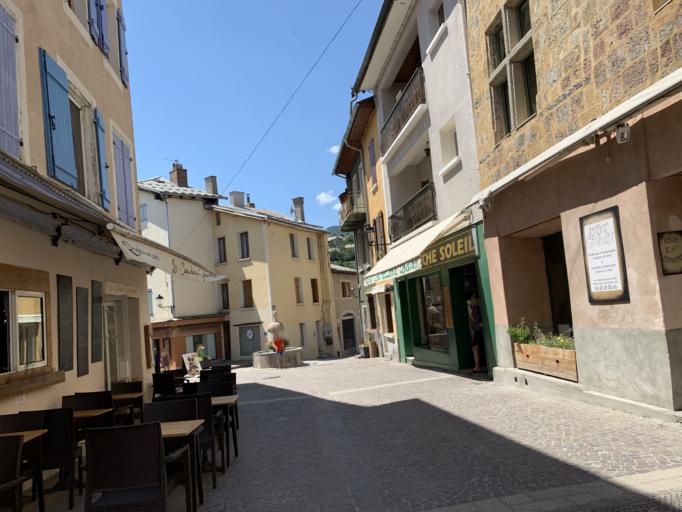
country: FR
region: Provence-Alpes-Cote d'Azur
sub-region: Departement des Hautes-Alpes
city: Embrun
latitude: 44.5636
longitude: 6.4942
